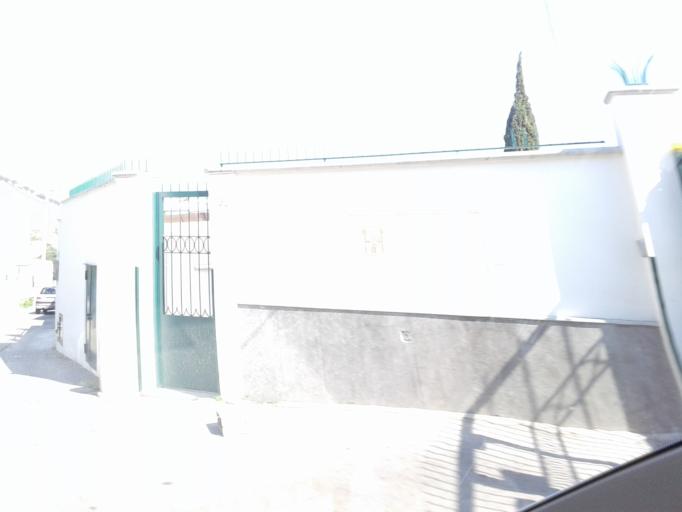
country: IT
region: Sicily
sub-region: Palermo
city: Piano dei Geli
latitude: 38.1112
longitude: 13.2984
